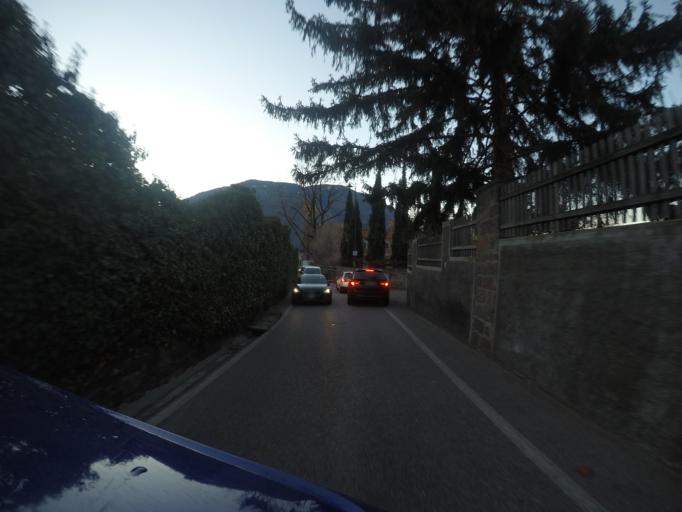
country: IT
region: Trentino-Alto Adige
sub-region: Bolzano
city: Bolzano
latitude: 46.5102
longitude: 11.3525
